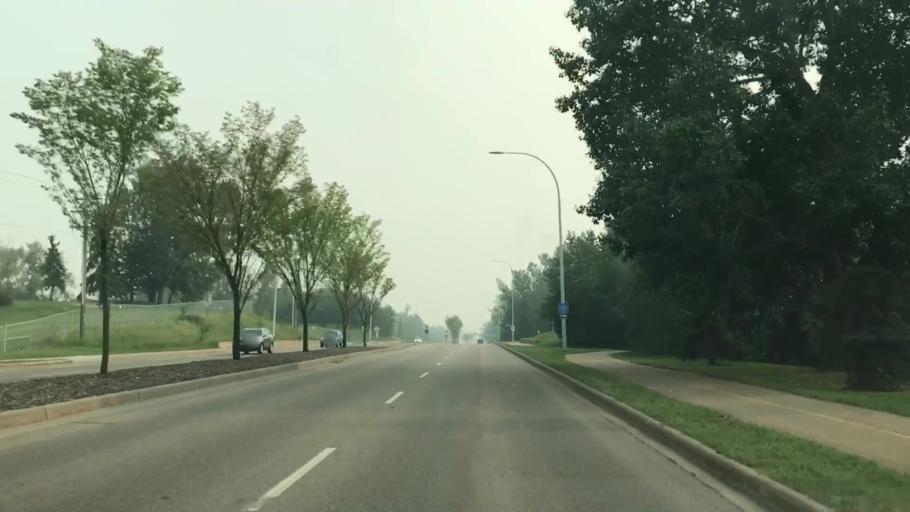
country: CA
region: Alberta
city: Sherwood Park
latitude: 53.5328
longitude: -113.3202
